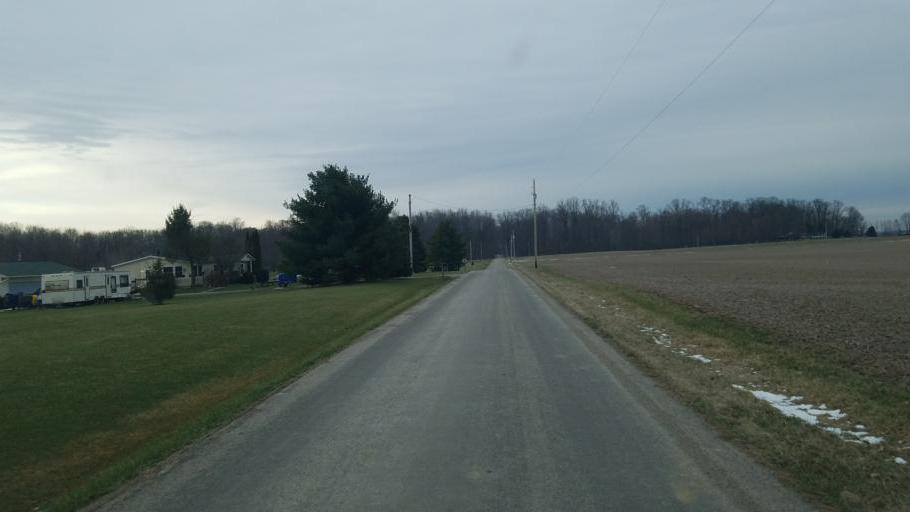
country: US
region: Ohio
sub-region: Morrow County
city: Mount Gilead
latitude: 40.5582
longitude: -82.7771
